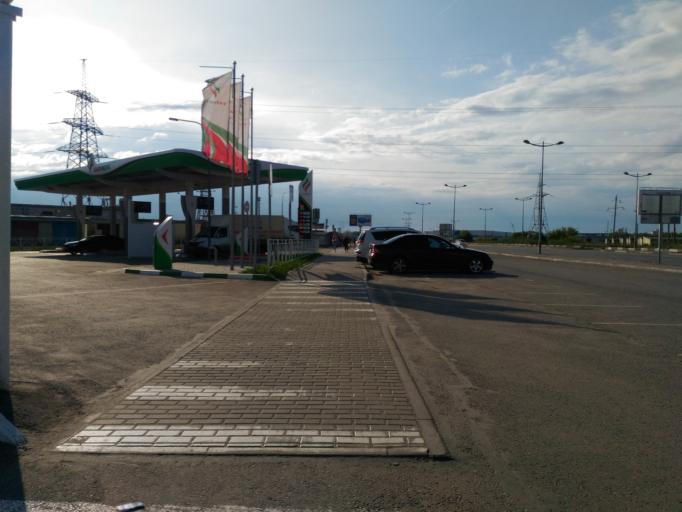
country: RU
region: Ulyanovsk
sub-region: Ulyanovskiy Rayon
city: Ulyanovsk
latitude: 54.2856
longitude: 48.2828
